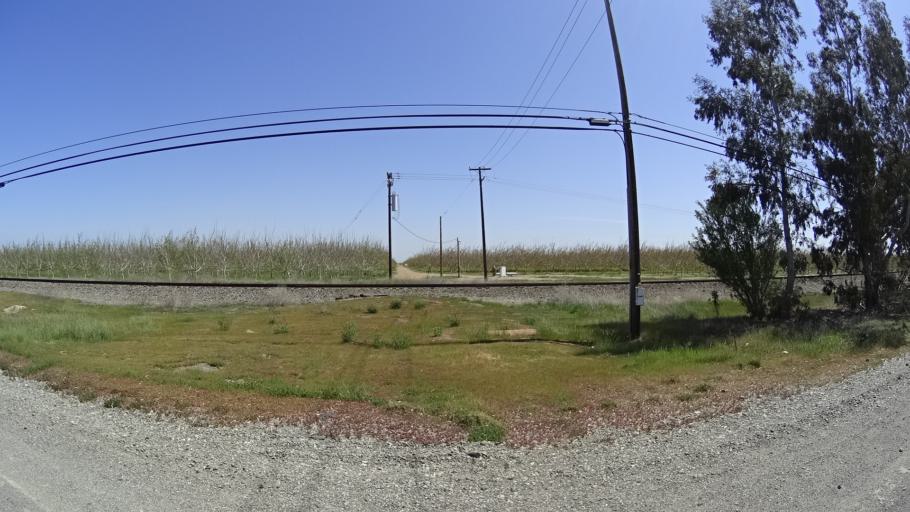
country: US
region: California
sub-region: Glenn County
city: Willows
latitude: 39.5968
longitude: -122.1940
